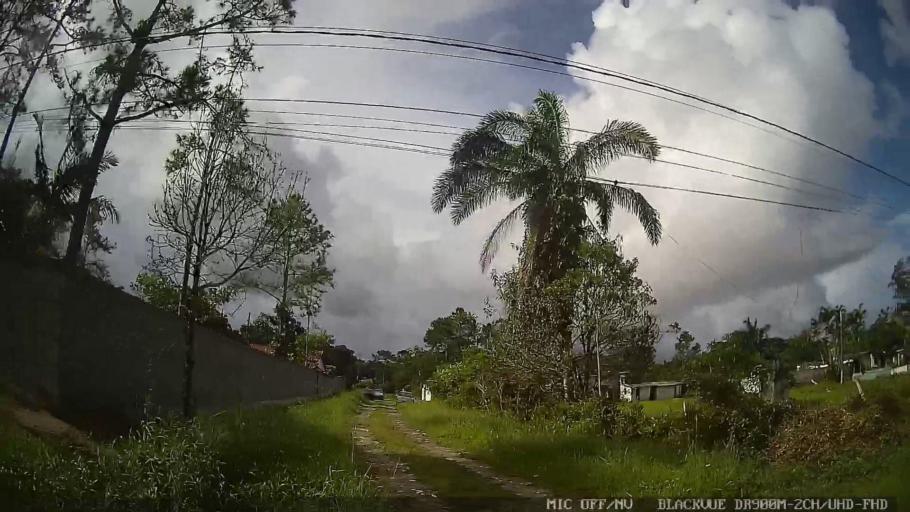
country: BR
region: Sao Paulo
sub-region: Itanhaem
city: Itanhaem
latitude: -24.2257
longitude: -46.8963
